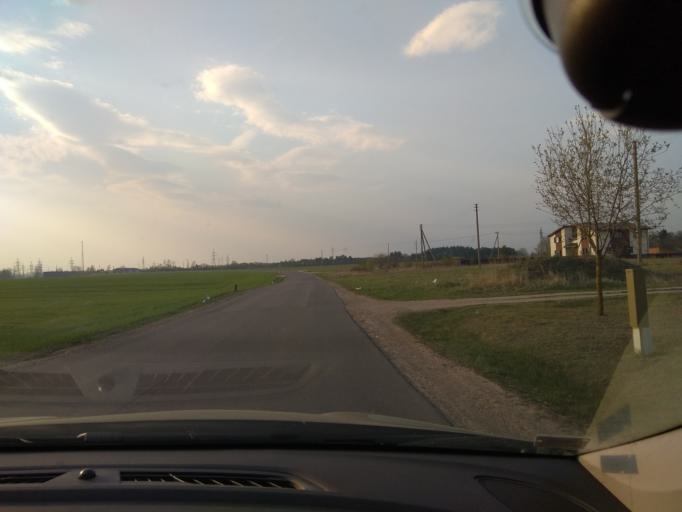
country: LT
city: Baltoji Voke
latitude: 54.6074
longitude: 25.1306
